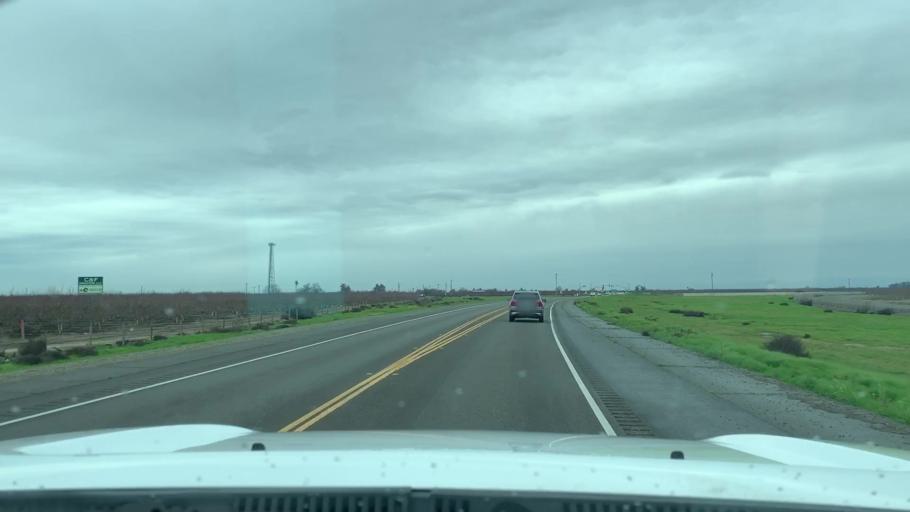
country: US
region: California
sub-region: Fresno County
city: Caruthers
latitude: 36.4839
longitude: -119.7918
